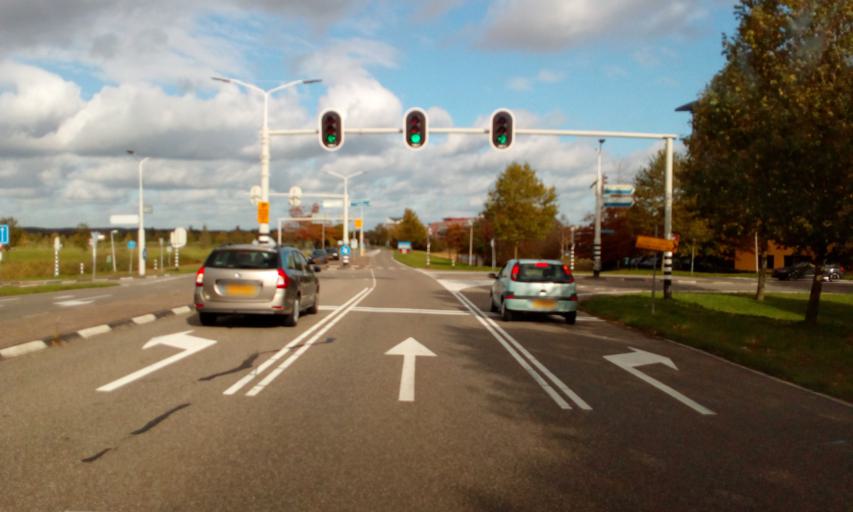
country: NL
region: South Holland
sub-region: Gemeente Hendrik-Ido-Ambacht
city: Hendrik-Ido-Ambacht
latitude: 51.8384
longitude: 4.6189
